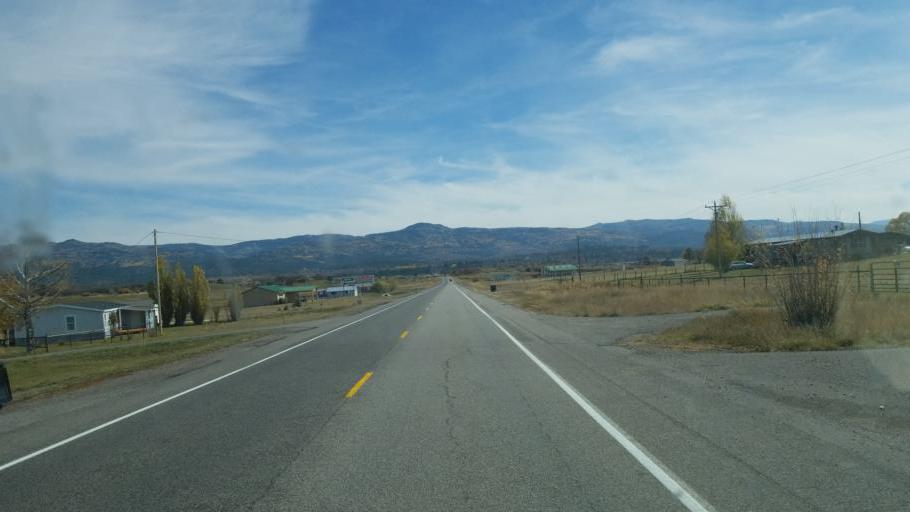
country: US
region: New Mexico
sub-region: Rio Arriba County
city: Chama
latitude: 36.8856
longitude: -106.6125
